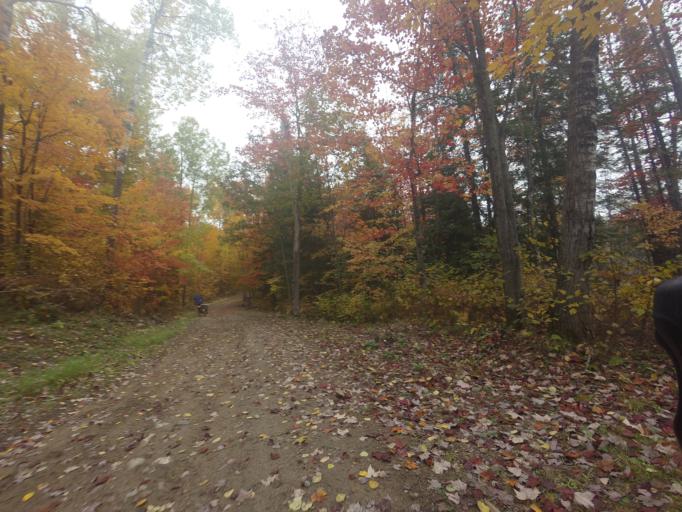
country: CA
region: Ontario
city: Petawawa
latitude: 45.7527
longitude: -77.3594
